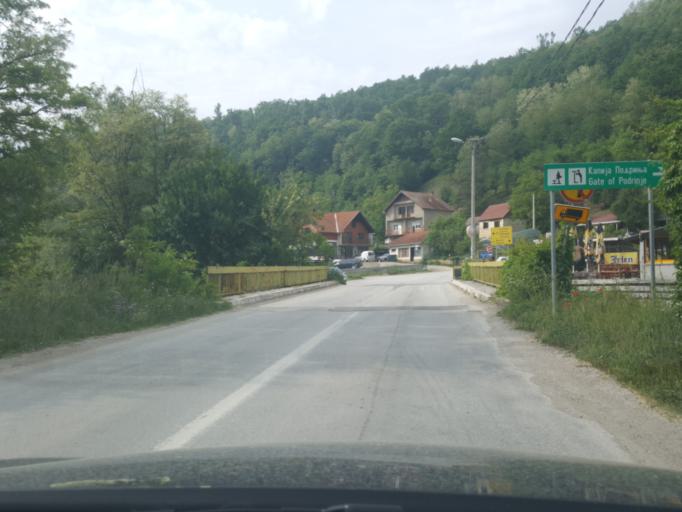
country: RS
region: Central Serbia
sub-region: Zlatiborski Okrug
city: Bajina Basta
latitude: 44.0400
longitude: 19.6254
